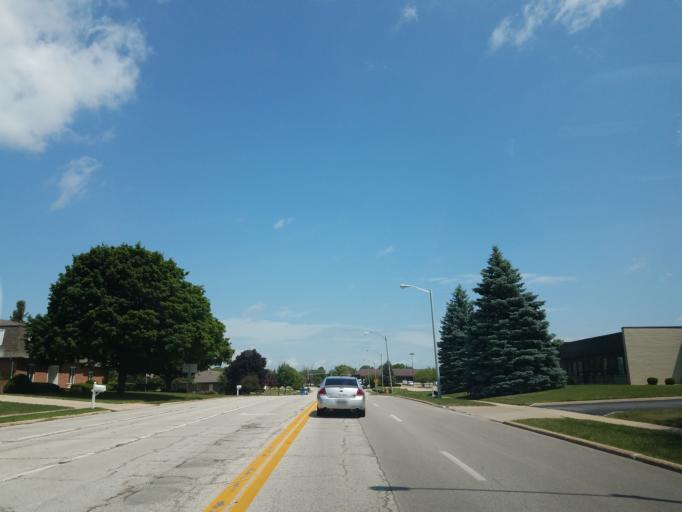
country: US
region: Illinois
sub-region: McLean County
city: Bloomington
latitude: 40.4841
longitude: -88.9609
